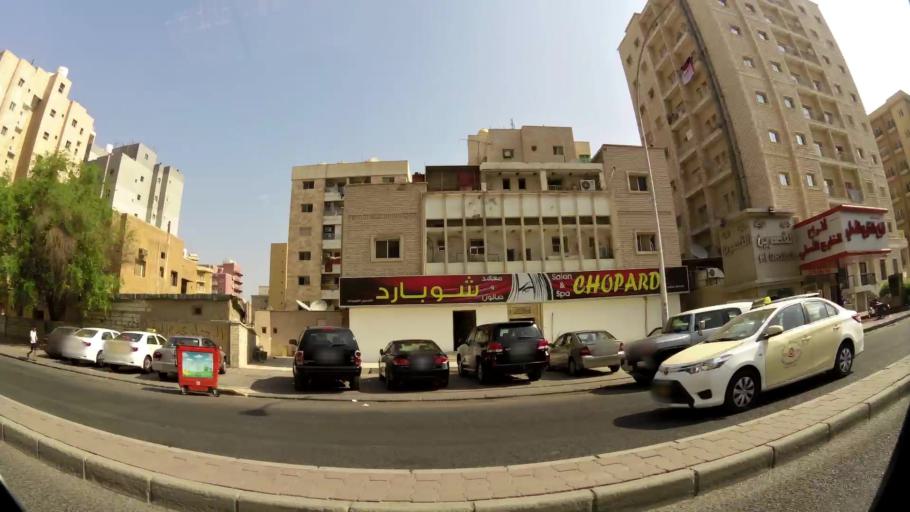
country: KW
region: Muhafazat Hawalli
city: Hawalli
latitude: 29.3344
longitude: 48.0081
